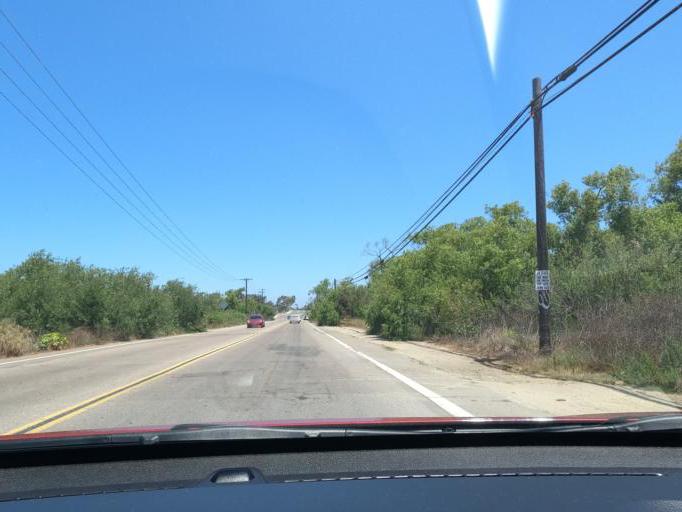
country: US
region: California
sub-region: San Diego County
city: Imperial Beach
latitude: 32.5548
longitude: -117.0624
